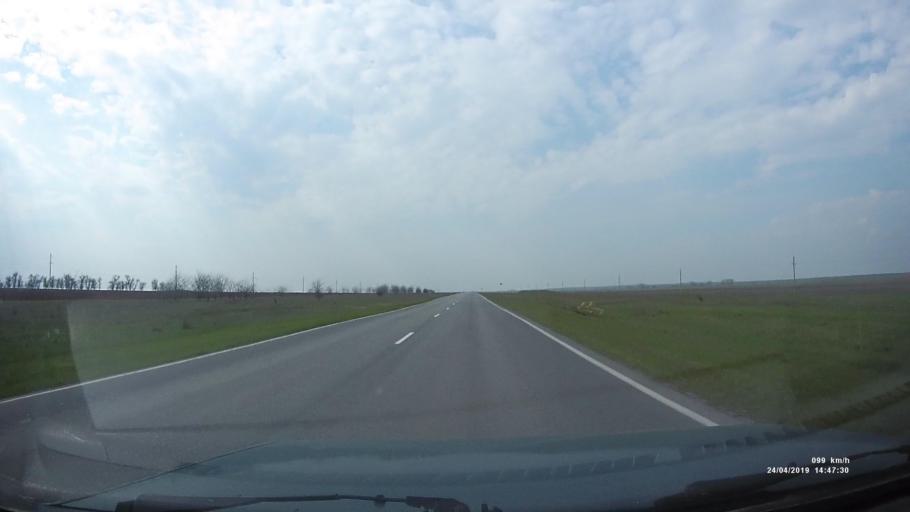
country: RU
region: Rostov
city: Remontnoye
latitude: 46.4929
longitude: 43.7710
